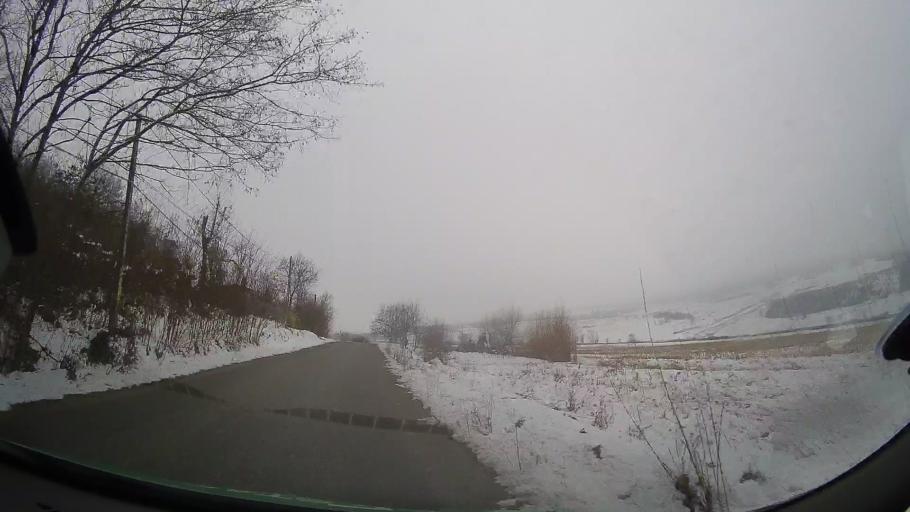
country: RO
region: Bacau
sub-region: Comuna Vultureni
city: Vultureni
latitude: 46.3393
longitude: 27.2907
